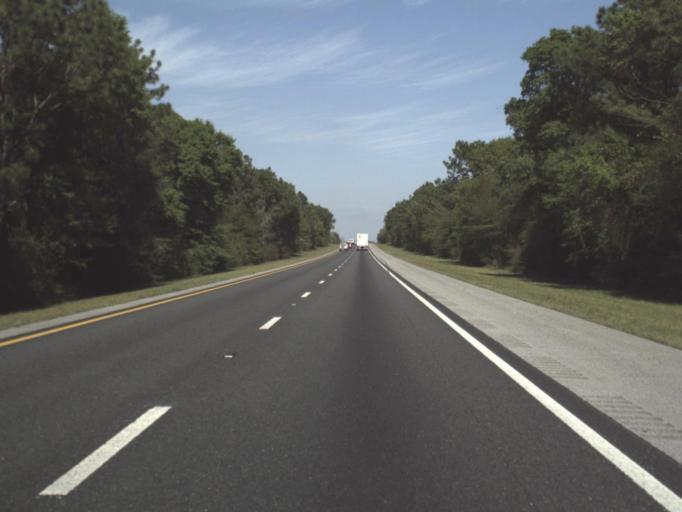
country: US
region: Florida
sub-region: Okaloosa County
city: Crestview
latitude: 30.7093
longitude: -86.7147
